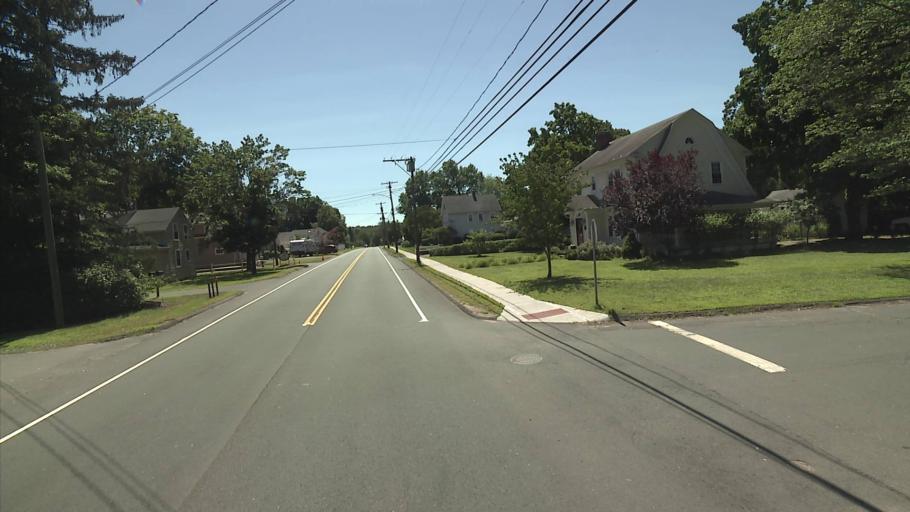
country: US
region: Connecticut
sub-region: New Haven County
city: Cheshire Village
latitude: 41.5684
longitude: -72.8950
